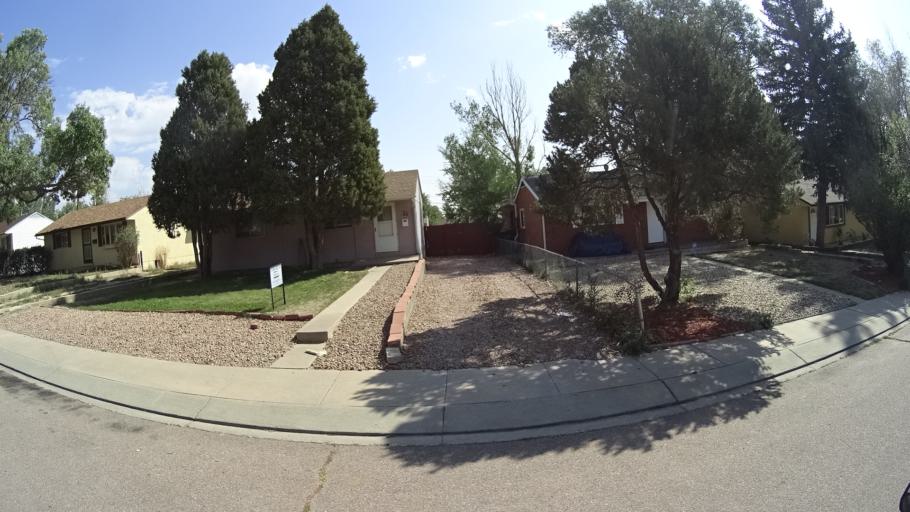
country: US
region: Colorado
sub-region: El Paso County
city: Colorado Springs
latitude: 38.8227
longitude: -104.7925
